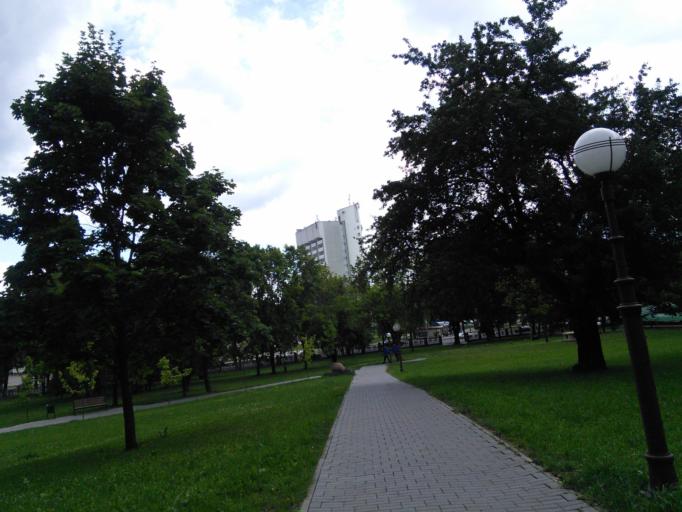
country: BY
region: Minsk
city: Maladzyechna
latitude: 54.3050
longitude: 26.8346
